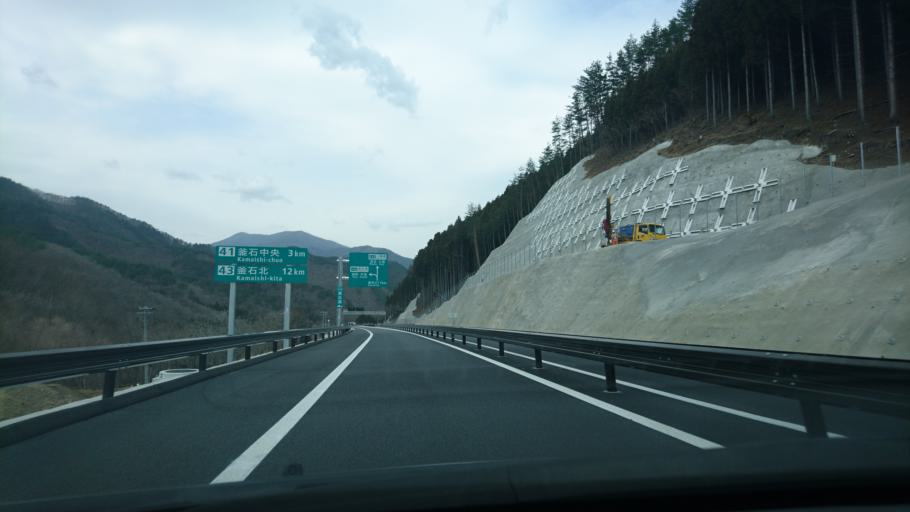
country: JP
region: Iwate
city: Kamaishi
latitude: 39.2442
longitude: 141.8443
